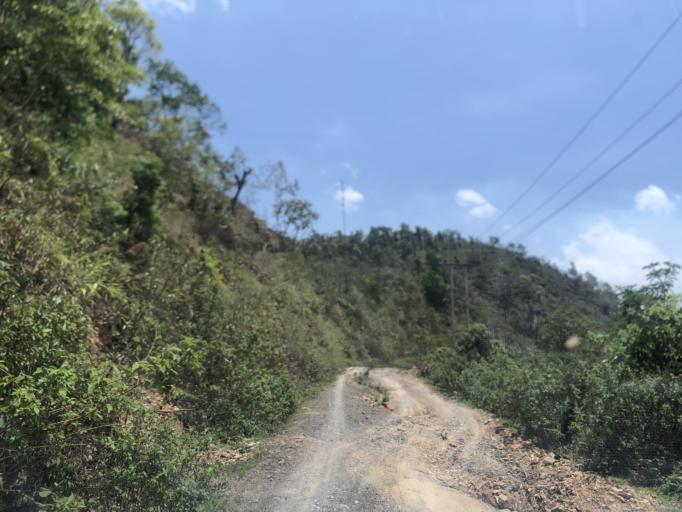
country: LA
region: Phongsali
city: Phongsali
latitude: 21.4389
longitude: 102.1619
